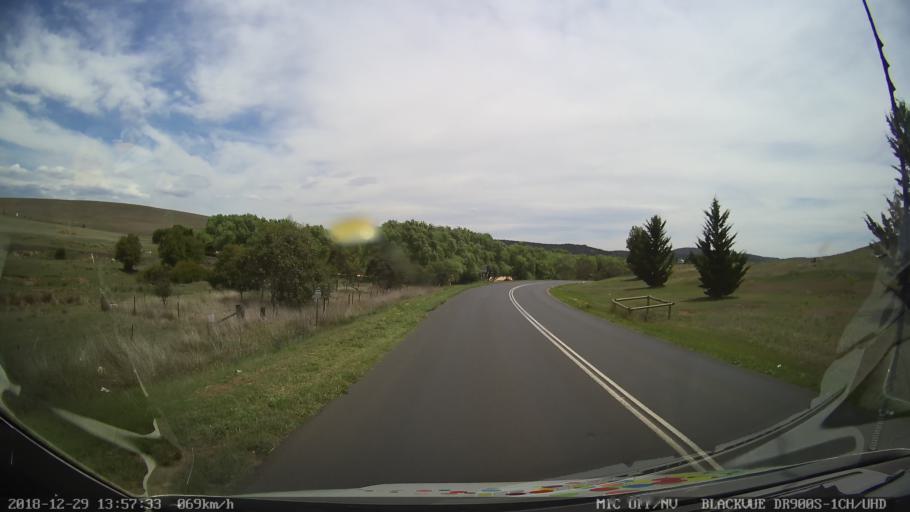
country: AU
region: New South Wales
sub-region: Cooma-Monaro
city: Cooma
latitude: -36.2409
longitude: 149.1407
